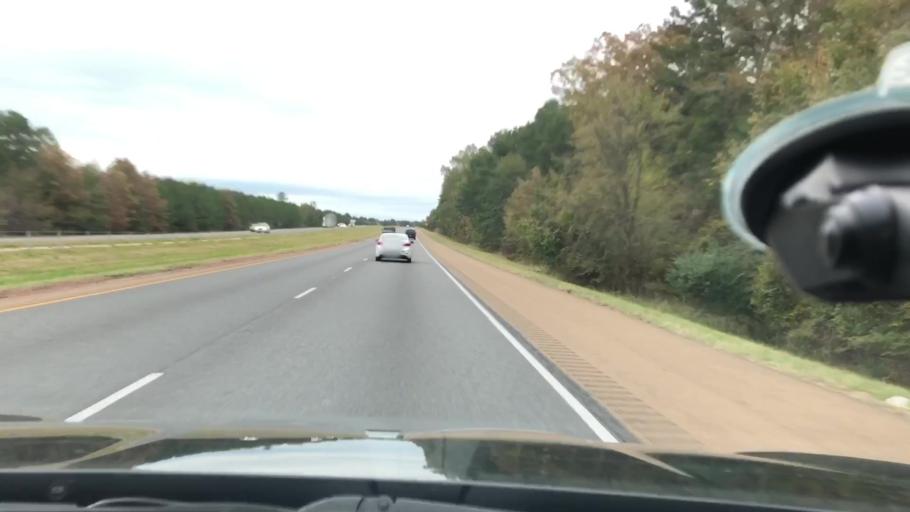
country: US
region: Arkansas
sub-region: Clark County
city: Gurdon
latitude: 33.9464
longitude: -93.2382
